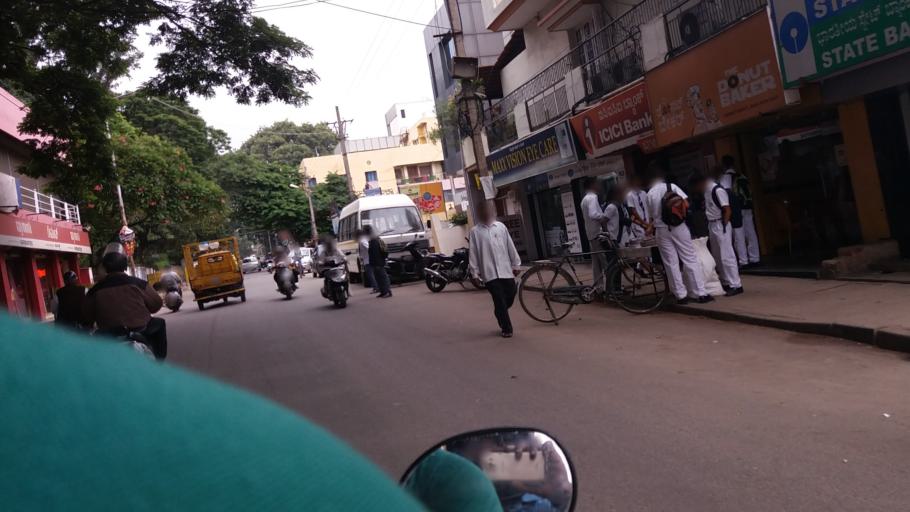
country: IN
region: Karnataka
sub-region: Bangalore Urban
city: Bangalore
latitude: 12.9718
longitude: 77.6273
